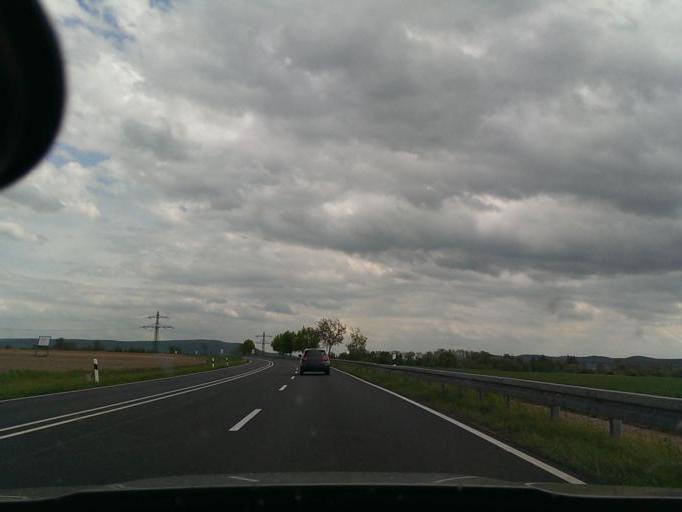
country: DE
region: Lower Saxony
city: Elze
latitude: 52.1115
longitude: 9.7215
